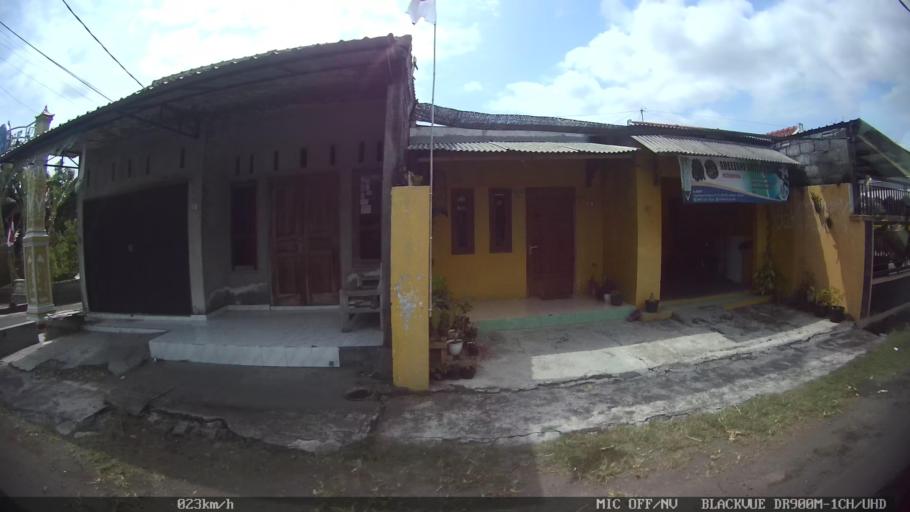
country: ID
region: Daerah Istimewa Yogyakarta
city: Depok
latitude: -7.7758
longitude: 110.4643
